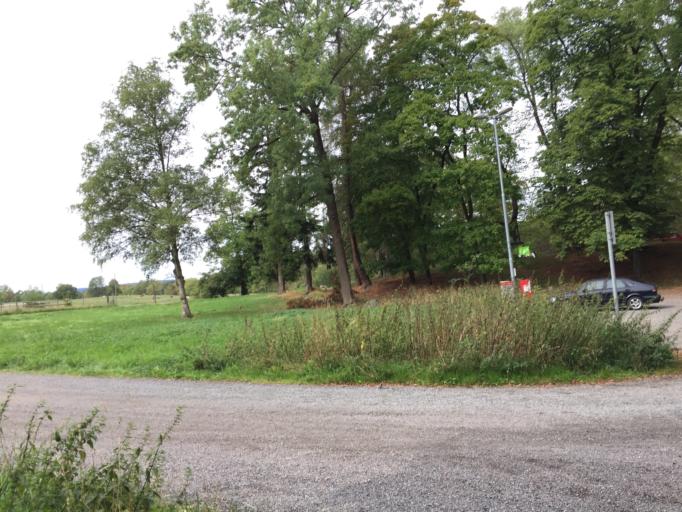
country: NO
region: Oslo
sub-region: Oslo
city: Sjolyststranda
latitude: 59.9137
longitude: 10.6897
